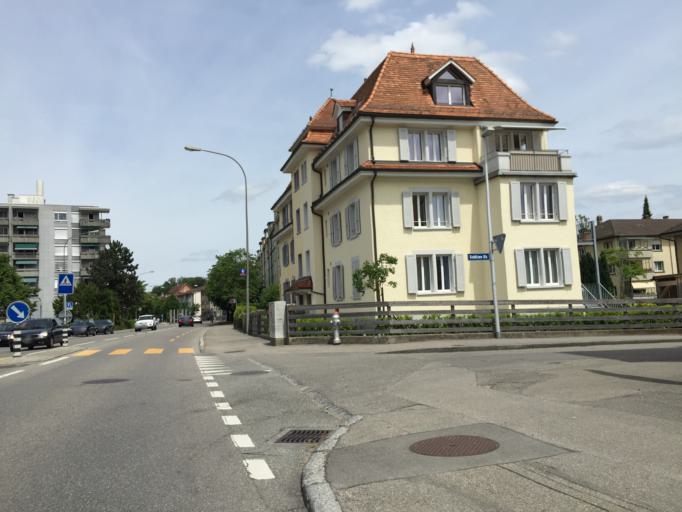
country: CH
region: Bern
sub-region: Bern-Mittelland District
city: Koniz
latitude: 46.9315
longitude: 7.4211
